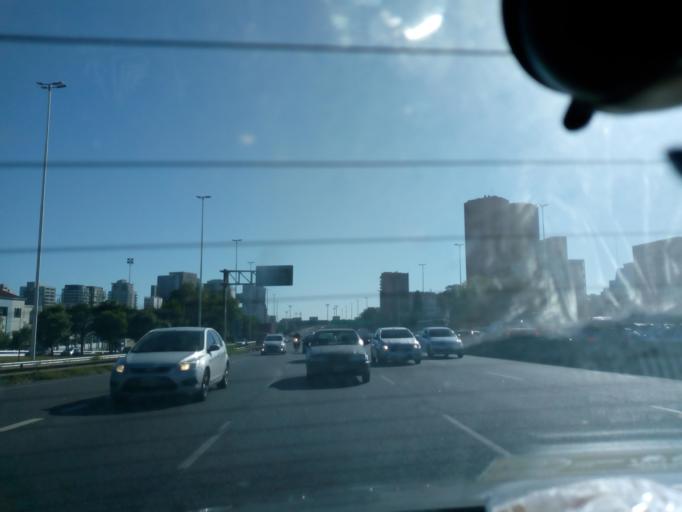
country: AR
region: Buenos Aires
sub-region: Partido de Vicente Lopez
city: Olivos
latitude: -34.5377
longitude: -58.4733
